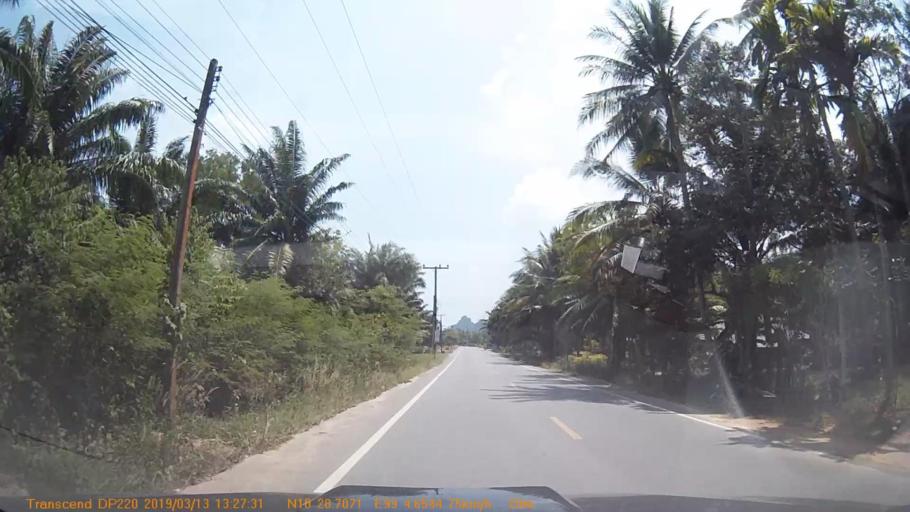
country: TH
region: Chumphon
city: Chumphon
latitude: 10.4838
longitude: 99.0768
